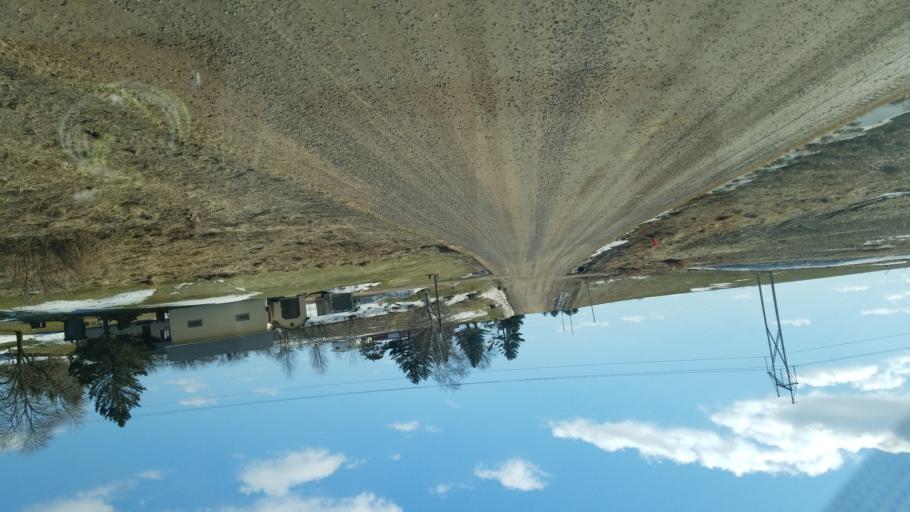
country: US
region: Wisconsin
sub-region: Clark County
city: Loyal
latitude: 44.6702
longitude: -90.4559
